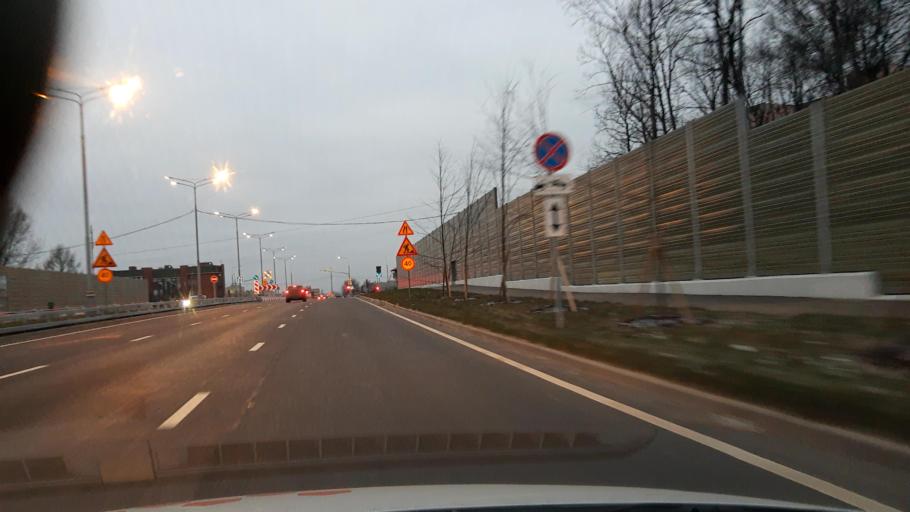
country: RU
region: Moskovskaya
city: Kommunarka
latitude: 55.5827
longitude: 37.4800
